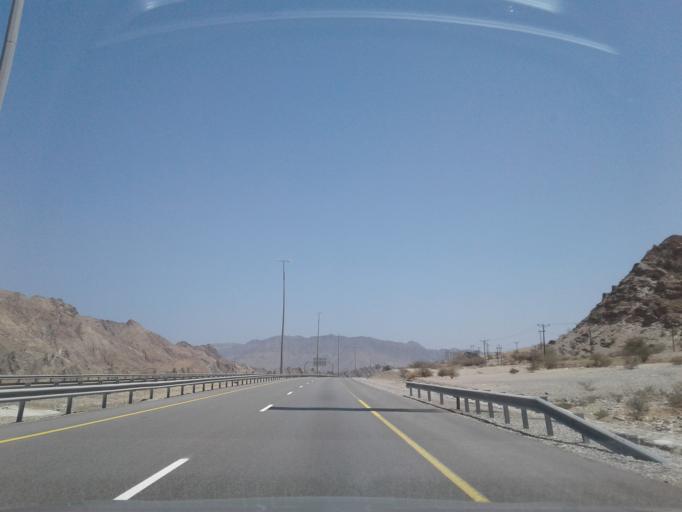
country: OM
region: Muhafazat Masqat
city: Muscat
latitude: 23.3536
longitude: 58.6830
